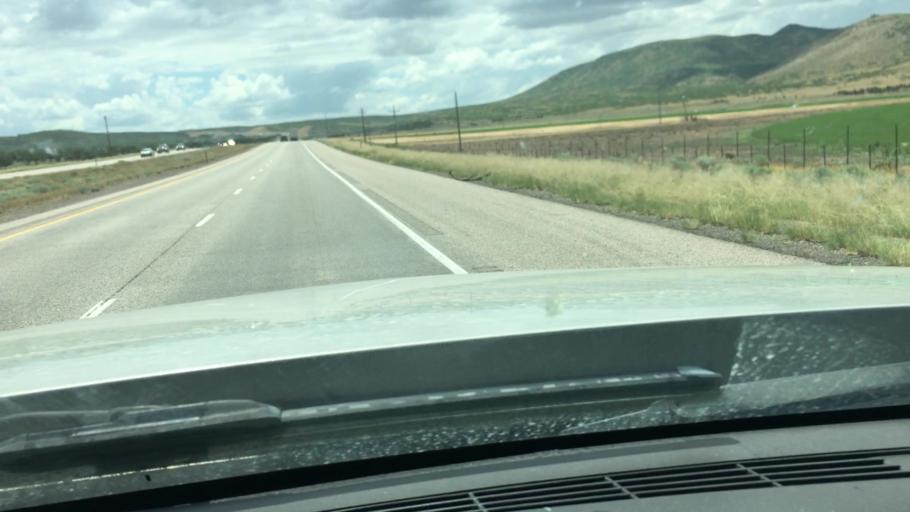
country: US
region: Utah
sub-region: Beaver County
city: Beaver
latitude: 38.5190
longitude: -112.6130
